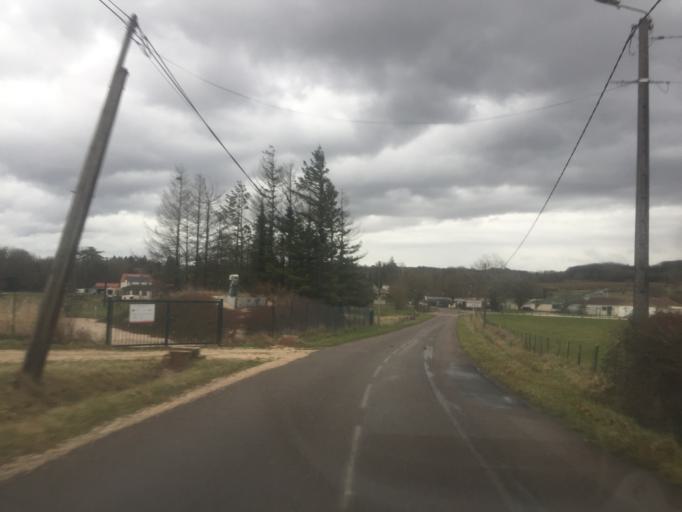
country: FR
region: Franche-Comte
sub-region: Departement de la Haute-Saone
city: Pesmes
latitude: 47.2187
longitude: 5.5129
